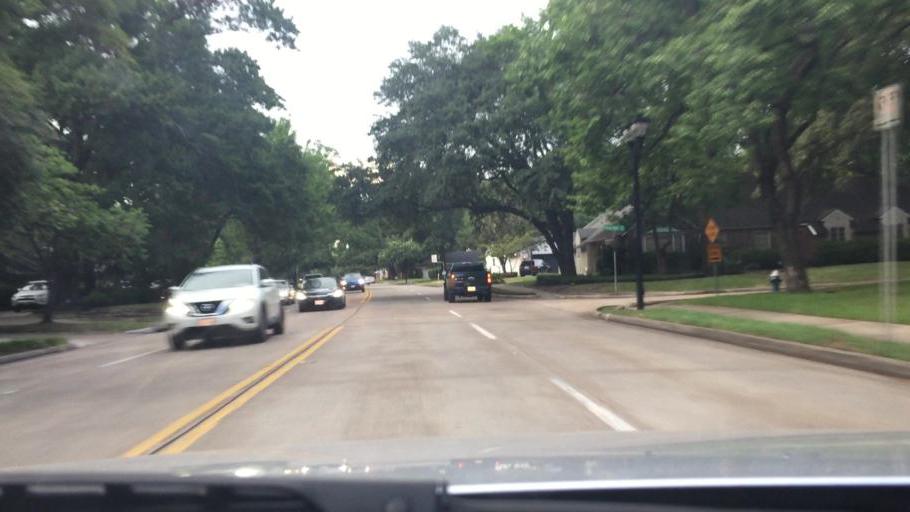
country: US
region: Texas
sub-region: Harris County
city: Hunters Creek Village
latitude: 29.7420
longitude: -95.4771
